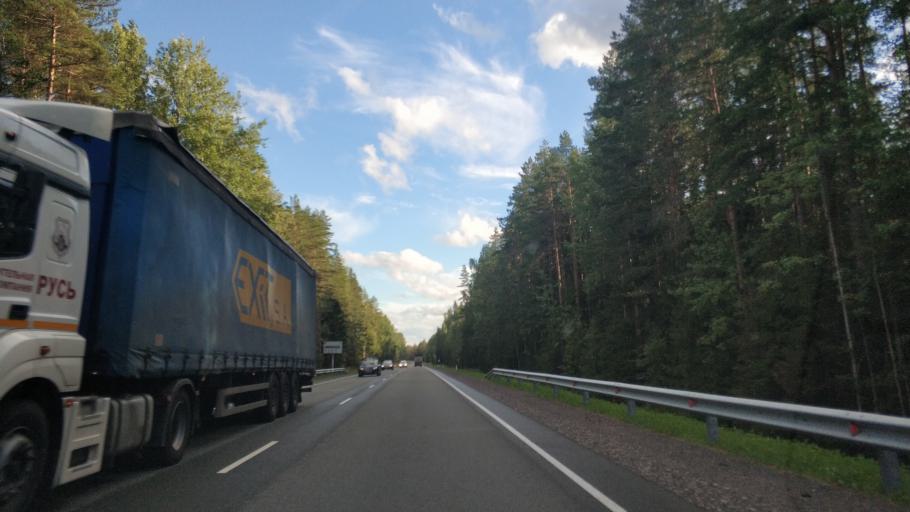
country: RU
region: Leningrad
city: Priozersk
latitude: 60.8988
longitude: 30.1598
